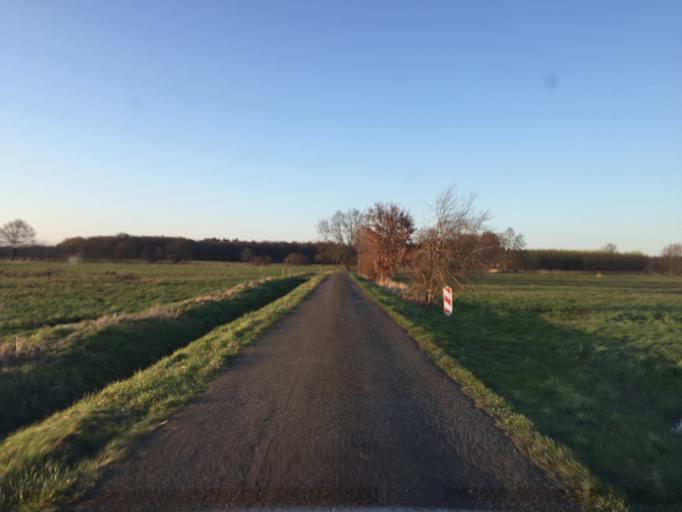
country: DE
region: Lower Saxony
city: Varrel
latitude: 52.6610
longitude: 8.7472
